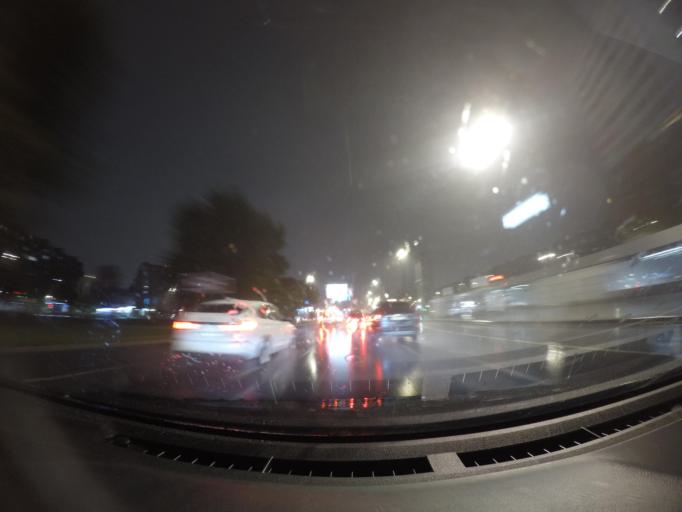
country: RU
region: Moskovskaya
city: Kozhukhovo
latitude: 55.6792
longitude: 37.6646
